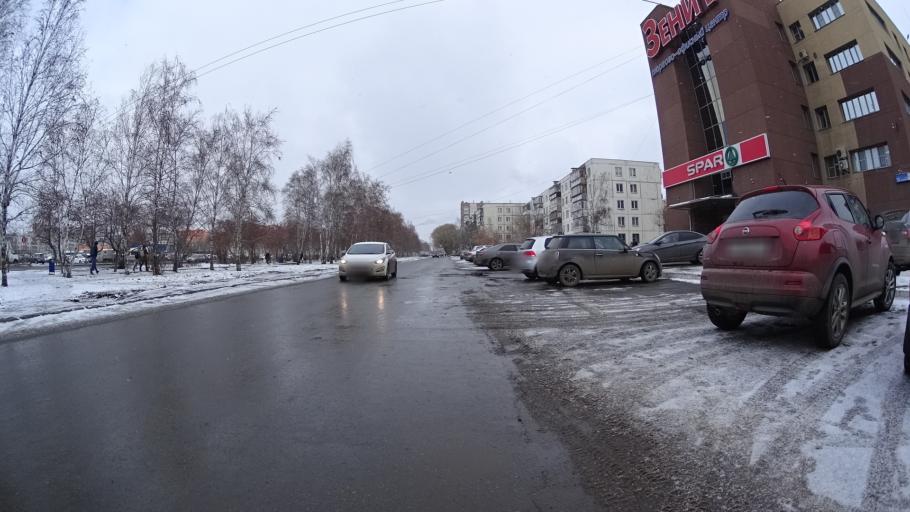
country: RU
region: Chelyabinsk
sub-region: Gorod Chelyabinsk
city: Chelyabinsk
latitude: 55.1917
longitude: 61.3219
